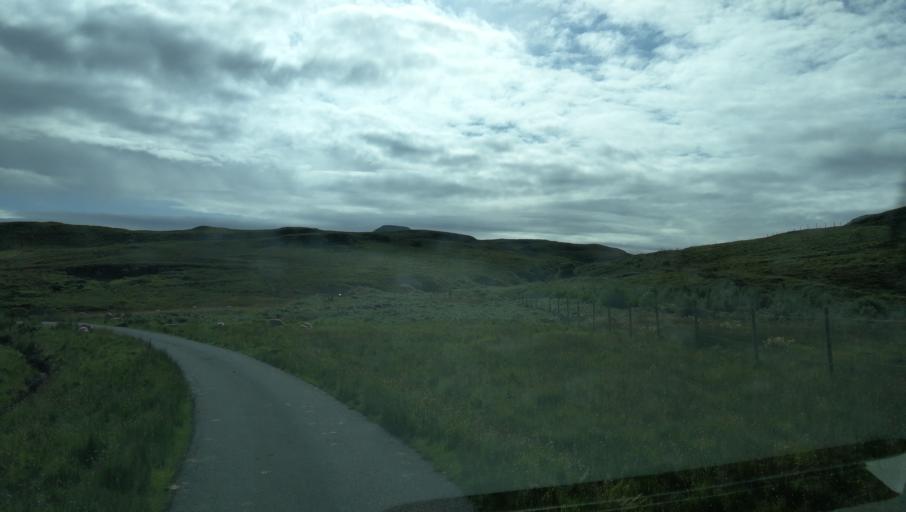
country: GB
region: Scotland
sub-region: Highland
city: Isle of Skye
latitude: 57.4077
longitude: -6.5704
